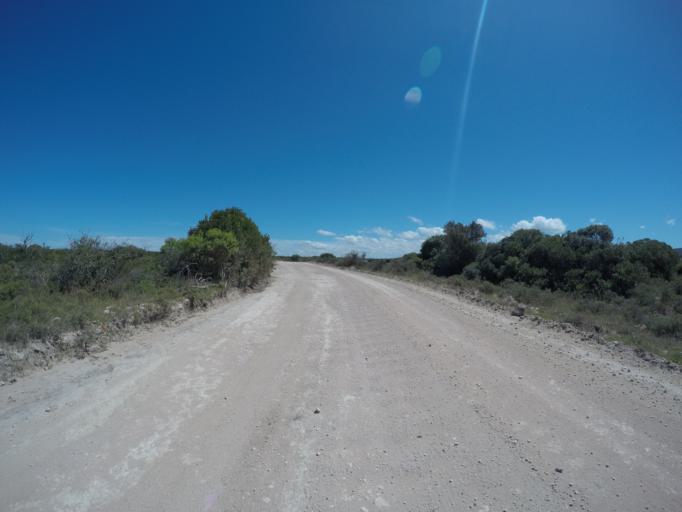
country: ZA
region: Western Cape
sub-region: Overberg District Municipality
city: Bredasdorp
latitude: -34.4559
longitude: 20.4171
